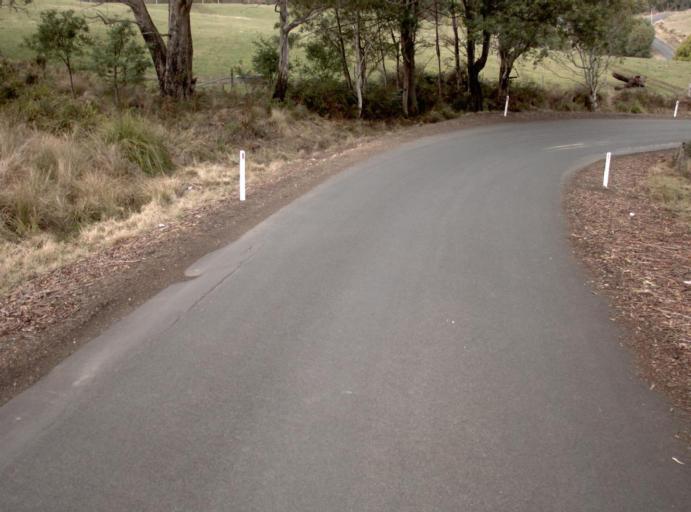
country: AU
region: Tasmania
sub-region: Dorset
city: Scottsdale
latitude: -41.4594
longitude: 147.5961
